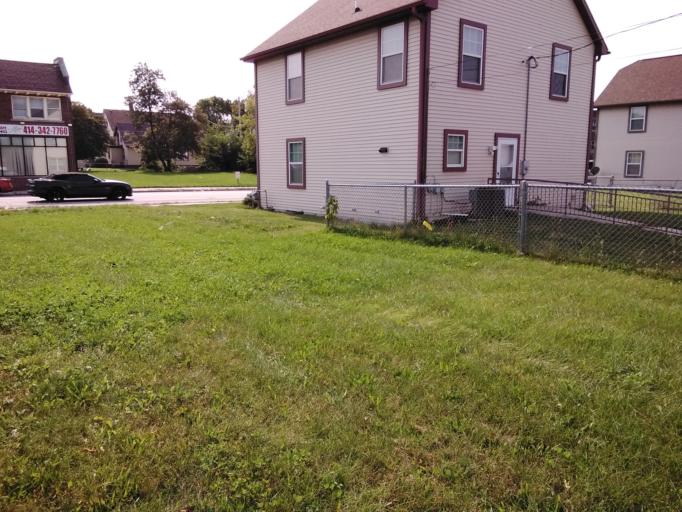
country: US
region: Wisconsin
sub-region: Milwaukee County
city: Milwaukee
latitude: 43.0489
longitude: -87.9445
